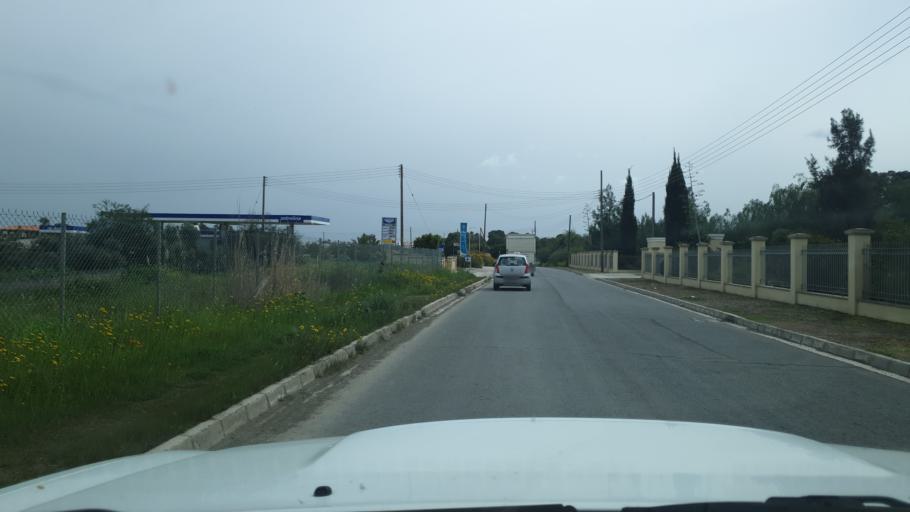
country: CY
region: Lefkosia
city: Tseri
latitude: 35.1058
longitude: 33.3635
